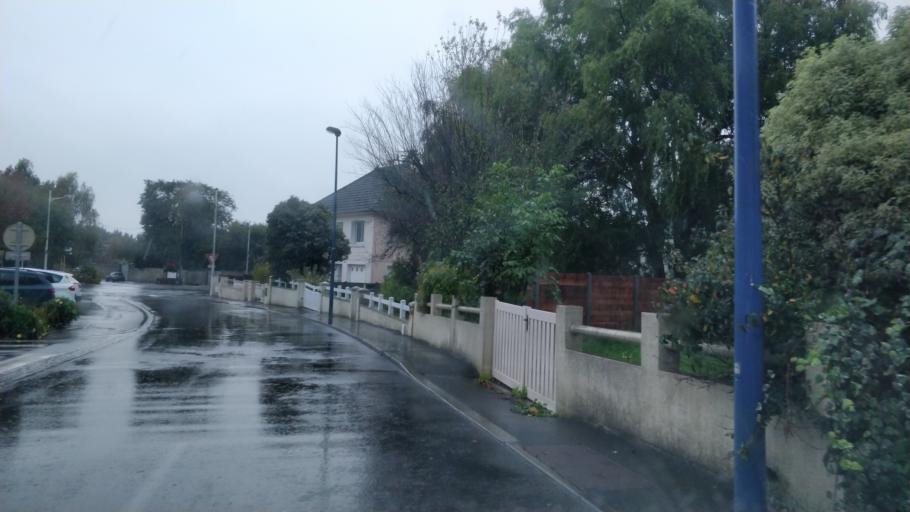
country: FR
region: Lower Normandy
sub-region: Departement de la Manche
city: Brehal
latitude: 48.8988
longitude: -1.5106
